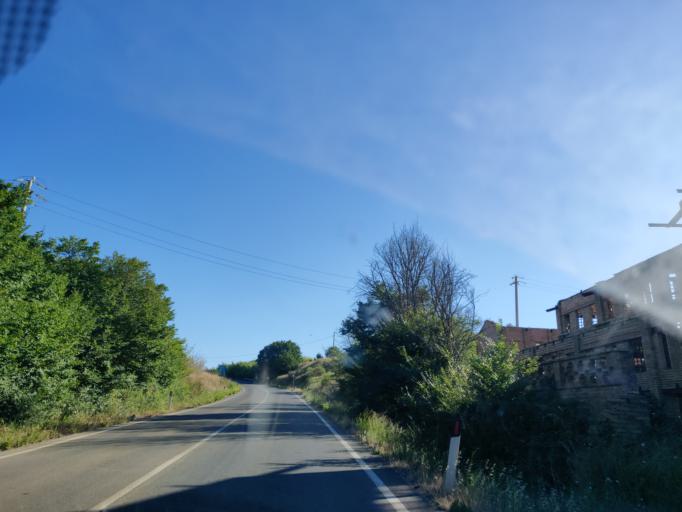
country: IT
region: Latium
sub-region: Citta metropolitana di Roma Capitale
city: Aurelia
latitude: 42.1514
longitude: 11.7887
